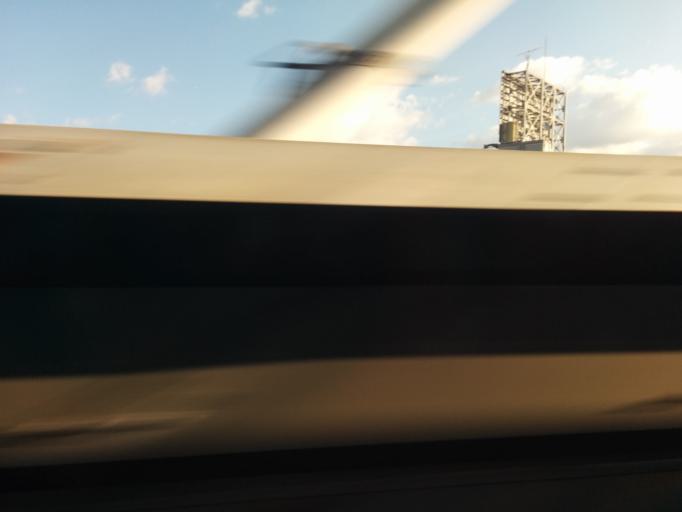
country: JP
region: Aichi
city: Nagoya-shi
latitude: 35.1101
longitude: 136.9078
